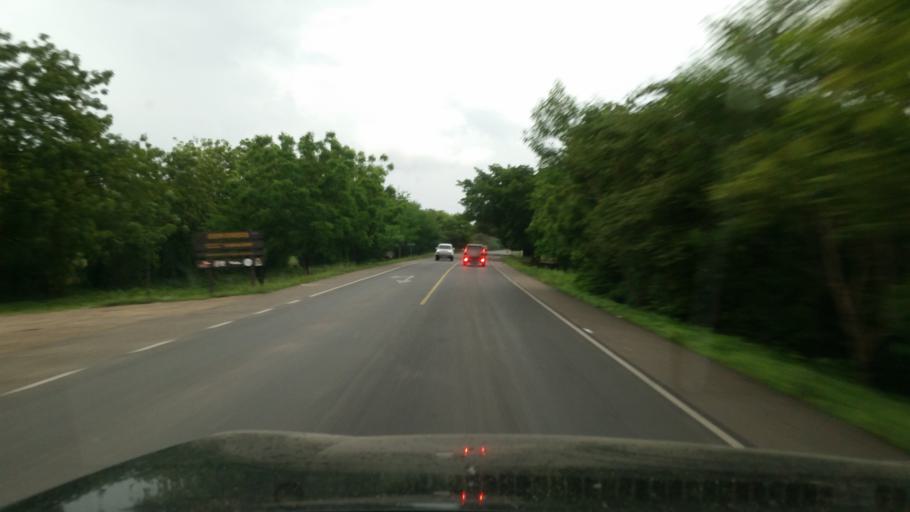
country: NI
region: Chinandega
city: Puerto Morazan
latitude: 12.7745
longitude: -87.0542
